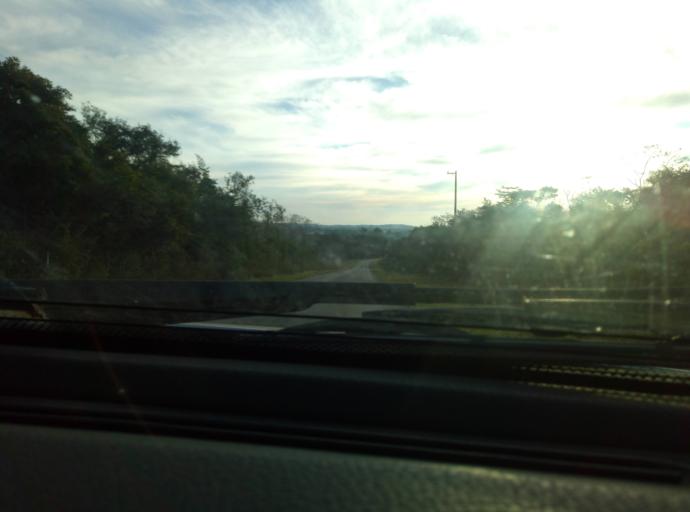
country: PY
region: Caaguazu
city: Carayao
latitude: -25.1526
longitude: -56.3280
